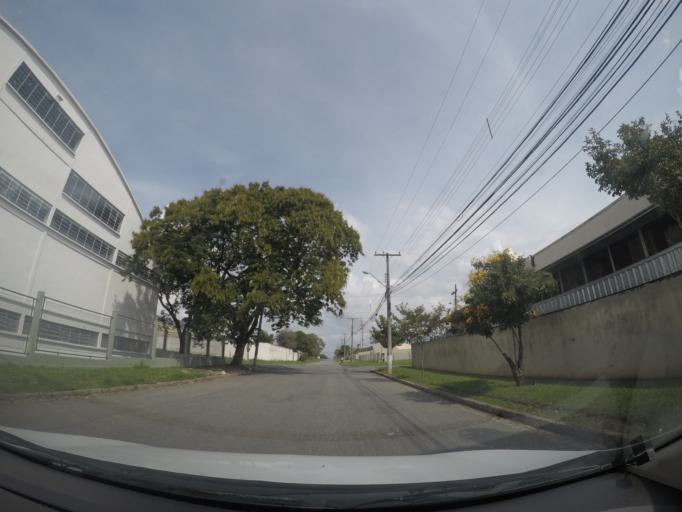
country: BR
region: Parana
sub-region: Curitiba
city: Curitiba
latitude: -25.4868
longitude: -49.2702
